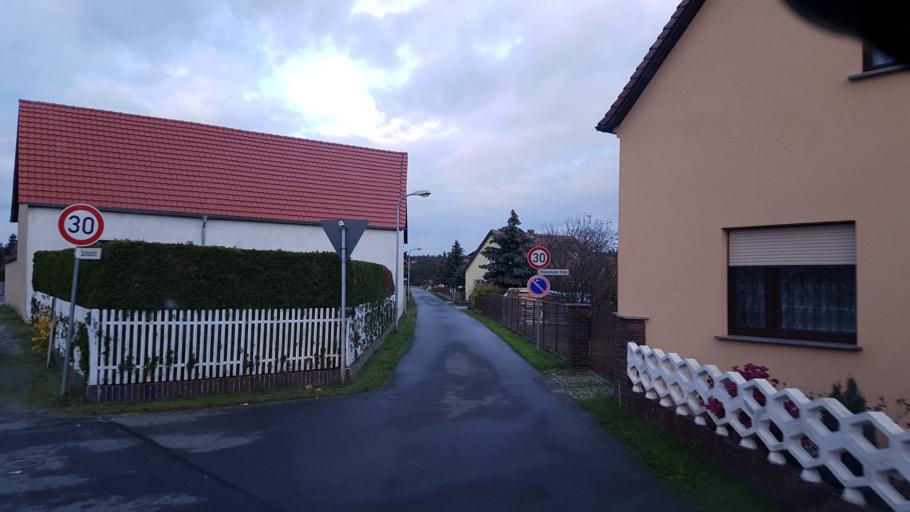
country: DE
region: Brandenburg
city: Tettau
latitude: 51.4180
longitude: 13.7695
